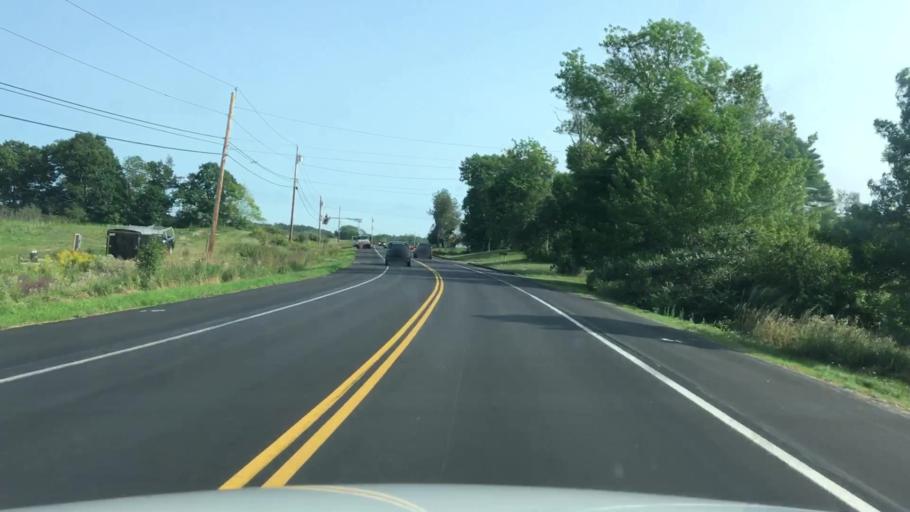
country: US
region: Maine
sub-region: Knox County
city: Warren
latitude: 44.1063
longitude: -69.2518
